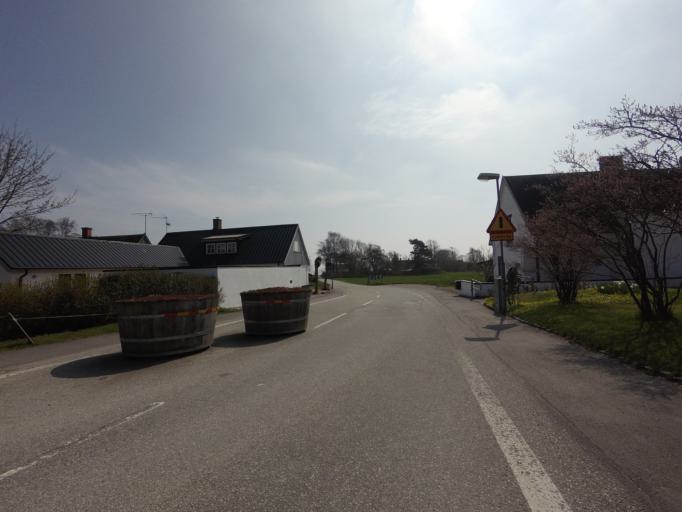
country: SE
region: Skane
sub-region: Skurups Kommun
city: Skivarp
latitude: 55.3923
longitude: 13.5958
